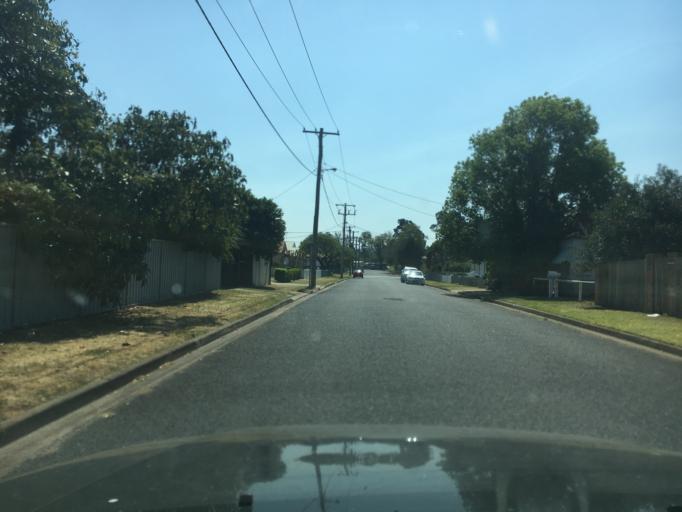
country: AU
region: New South Wales
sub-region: Singleton
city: Singleton
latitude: -32.5612
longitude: 151.1772
